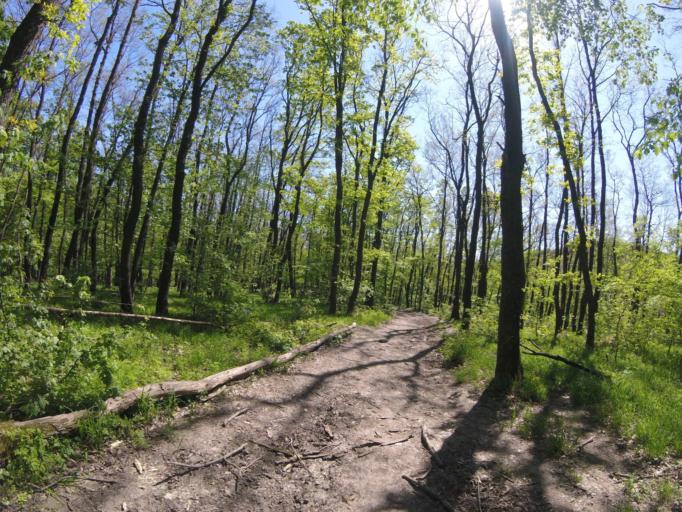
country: HU
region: Pest
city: Nagymaros
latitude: 47.7907
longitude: 18.9311
